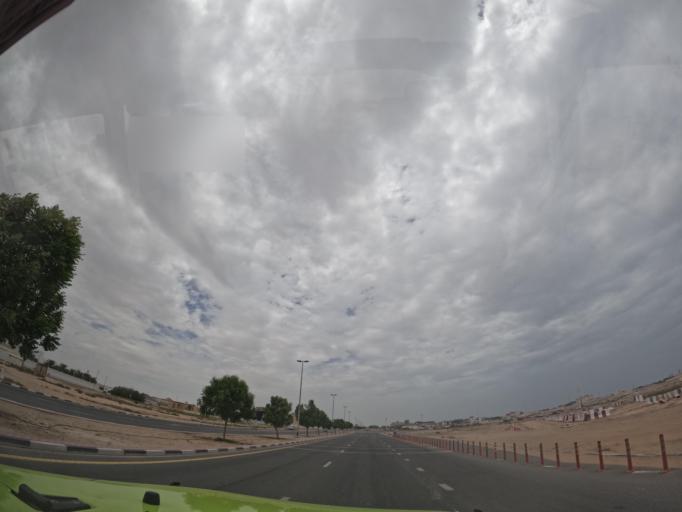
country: AE
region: Ash Shariqah
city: Sharjah
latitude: 25.1502
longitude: 55.3556
